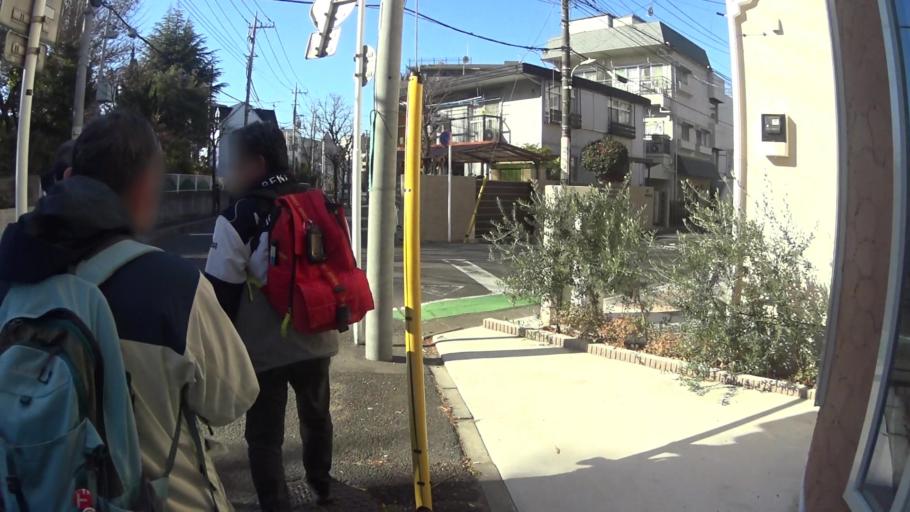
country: JP
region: Saitama
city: Shimotoda
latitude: 35.8534
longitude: 139.6680
